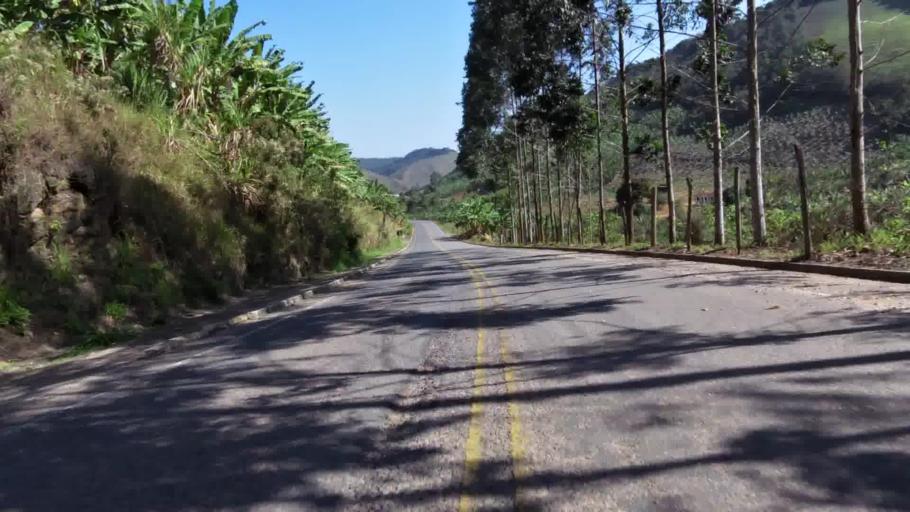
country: BR
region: Espirito Santo
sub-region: Alfredo Chaves
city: Alfredo Chaves
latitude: -20.5600
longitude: -40.8023
